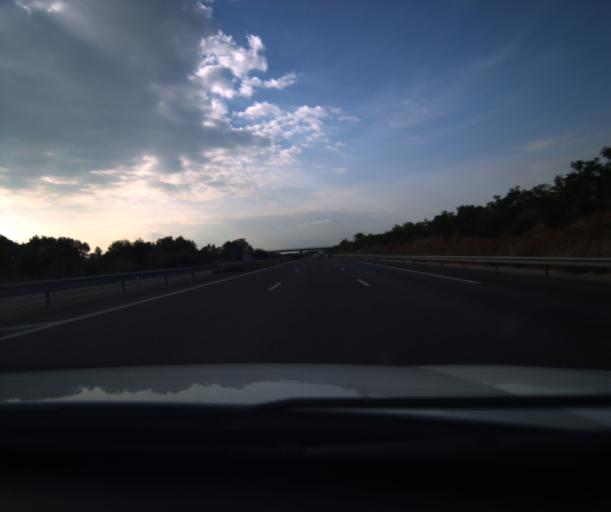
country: FR
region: Midi-Pyrenees
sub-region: Departement du Tarn-et-Garonne
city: Pompignan
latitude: 43.8284
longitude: 1.3431
